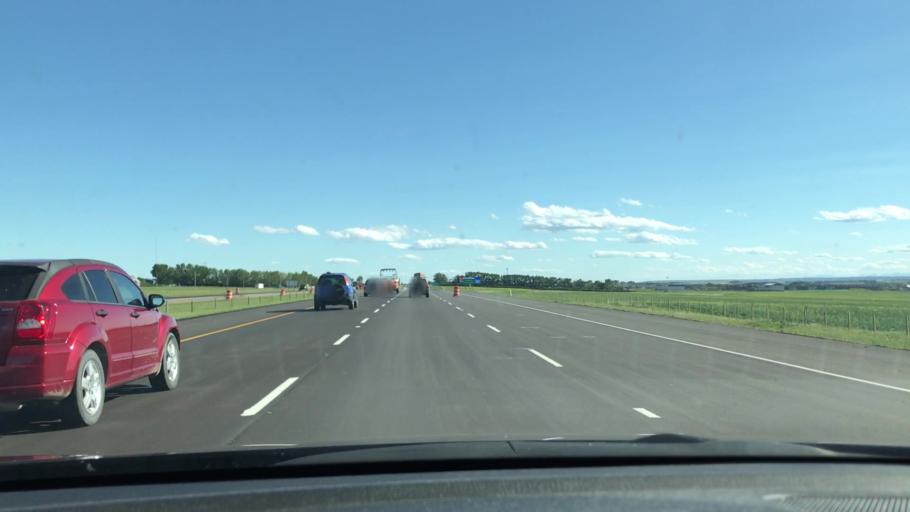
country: CA
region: Alberta
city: Airdrie
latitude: 51.3180
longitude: -114.0022
